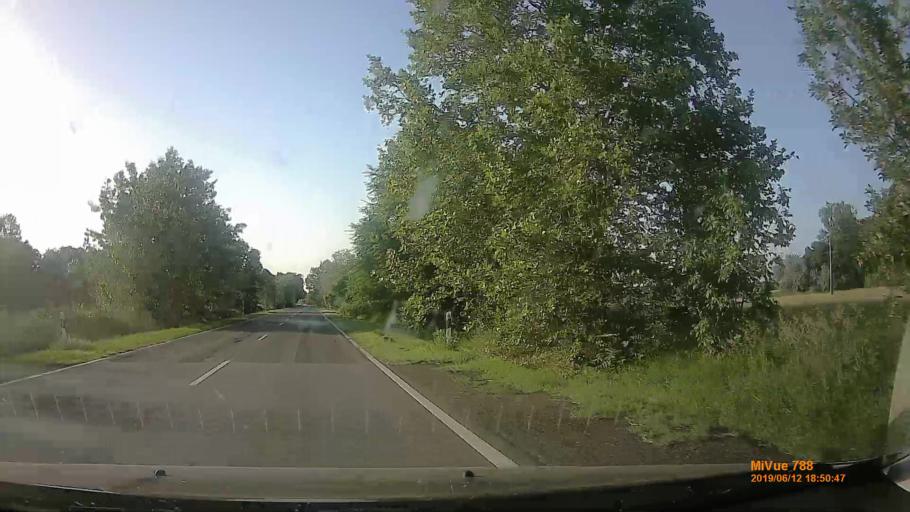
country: HU
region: Bacs-Kiskun
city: Kiskunfelegyhaza
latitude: 46.6519
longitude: 19.8742
